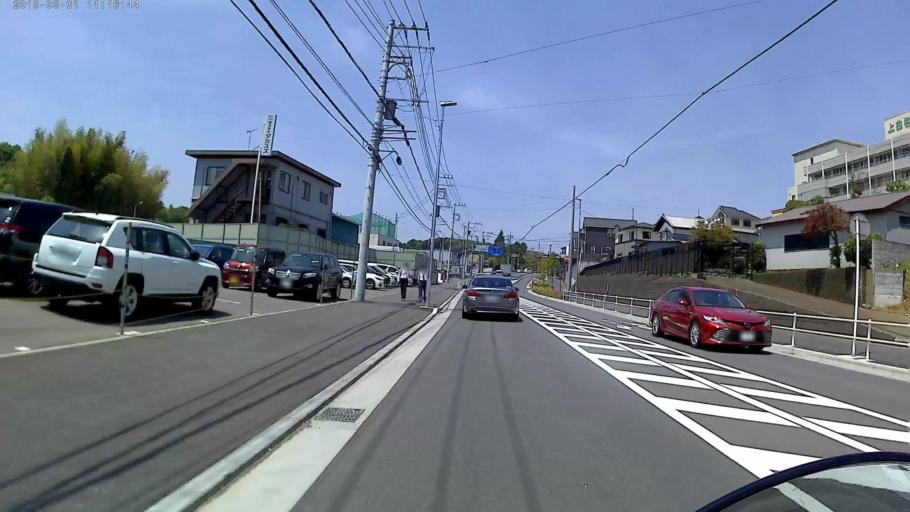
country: JP
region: Kanagawa
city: Minami-rinkan
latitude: 35.4932
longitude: 139.5350
